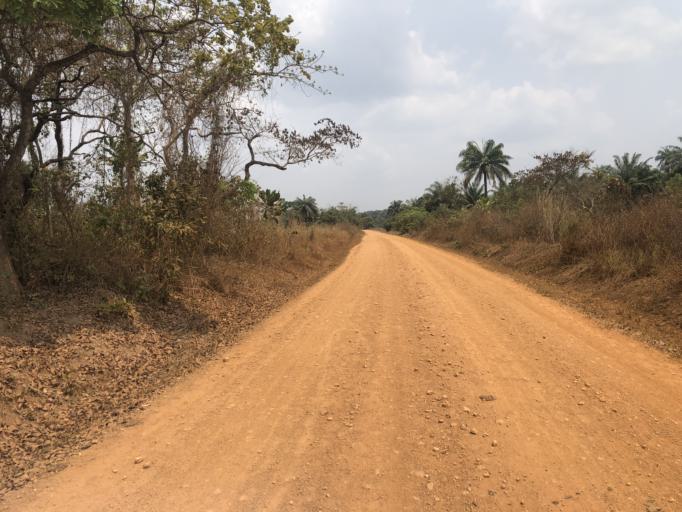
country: NG
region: Osun
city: Bode Osi
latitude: 7.7554
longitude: 4.2415
